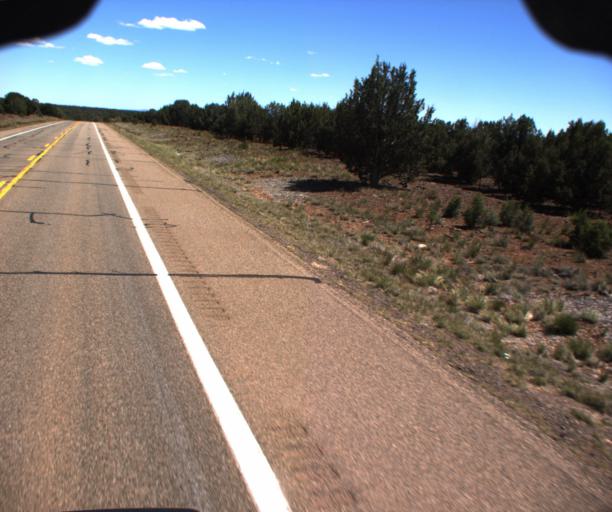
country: US
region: Arizona
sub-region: Yavapai County
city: Paulden
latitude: 35.0895
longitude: -112.4131
